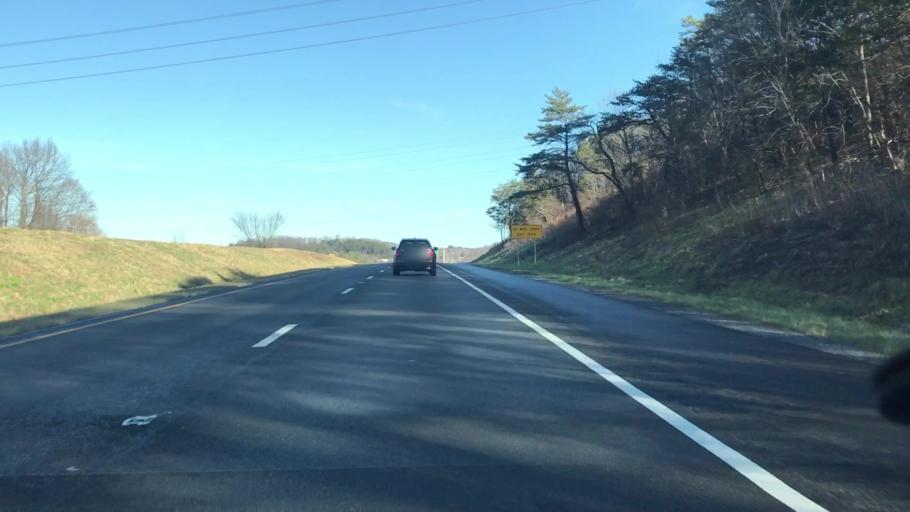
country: US
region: Virginia
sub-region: Botetourt County
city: Cloverdale
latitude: 37.3824
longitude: -79.9071
